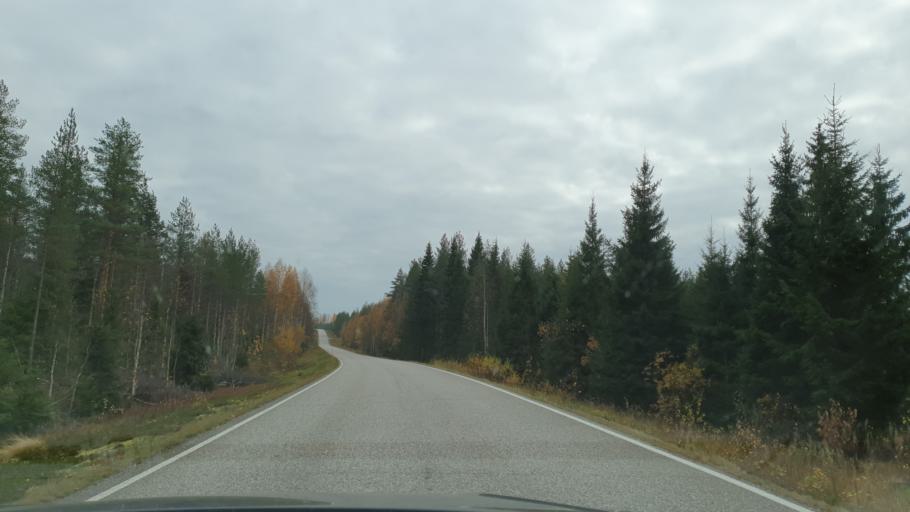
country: FI
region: Kainuu
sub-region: Kajaani
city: Ristijaervi
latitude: 64.6117
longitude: 27.9964
